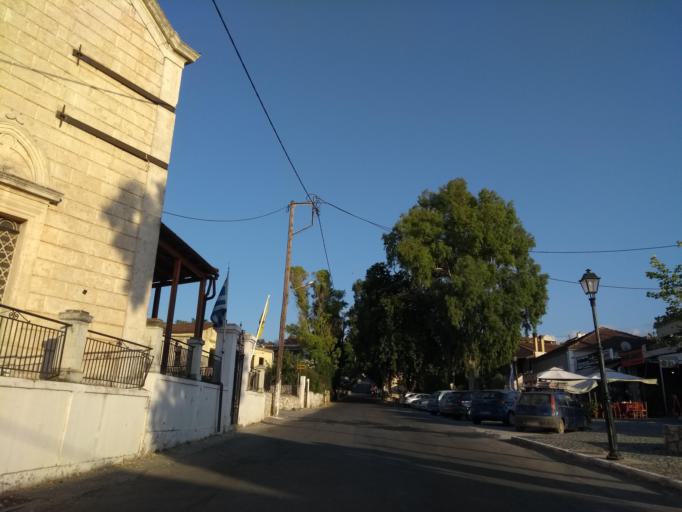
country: GR
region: Crete
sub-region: Nomos Chanias
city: Kalivai
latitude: 35.4098
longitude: 24.1970
